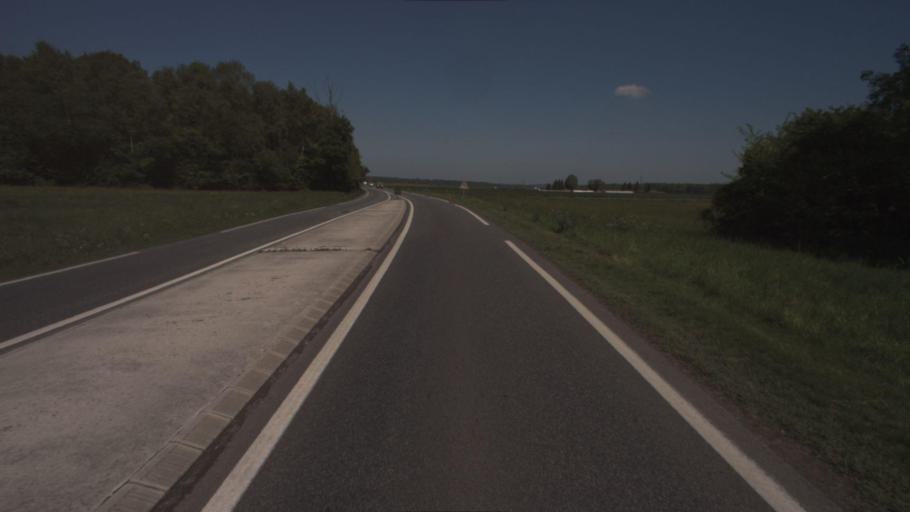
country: FR
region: Ile-de-France
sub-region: Departement de Seine-et-Marne
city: Voulangis
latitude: 48.8329
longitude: 2.8791
